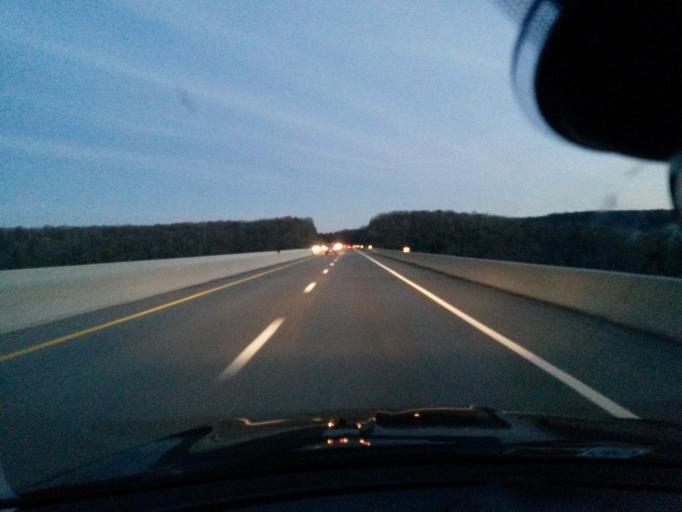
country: US
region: West Virginia
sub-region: Raleigh County
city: Shady Spring
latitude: 37.7699
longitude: -81.0431
